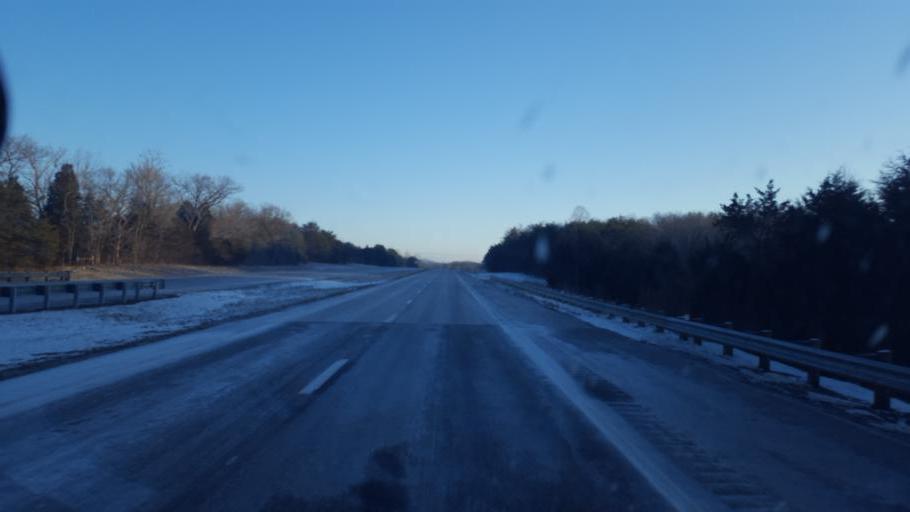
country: US
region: Ohio
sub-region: Adams County
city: Peebles
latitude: 38.9698
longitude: -83.3466
